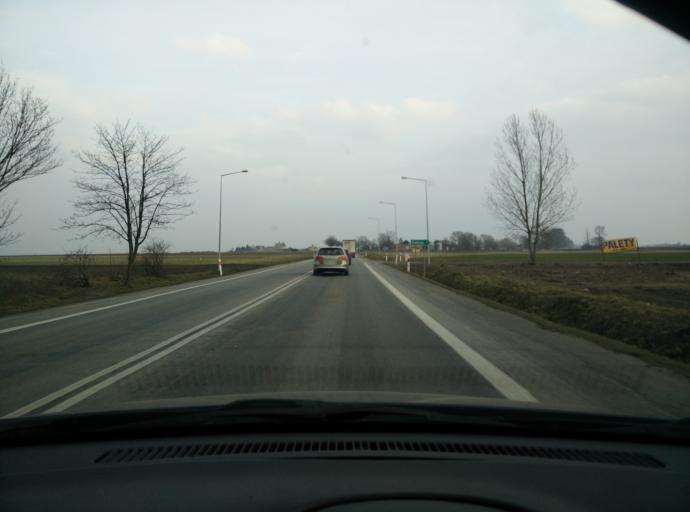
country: PL
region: Greater Poland Voivodeship
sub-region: Powiat poznanski
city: Kornik
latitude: 52.2384
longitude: 17.1573
